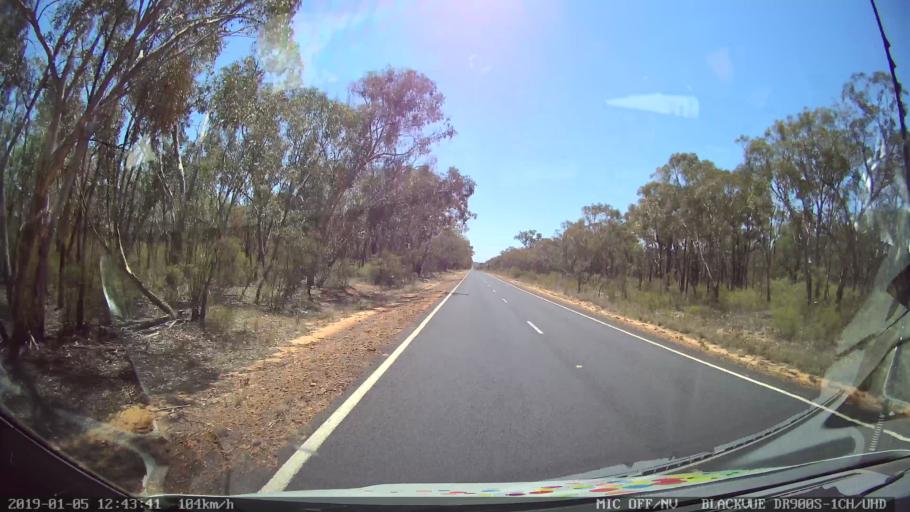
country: AU
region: New South Wales
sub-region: Warrumbungle Shire
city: Coonabarabran
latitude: -31.1455
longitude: 149.5273
